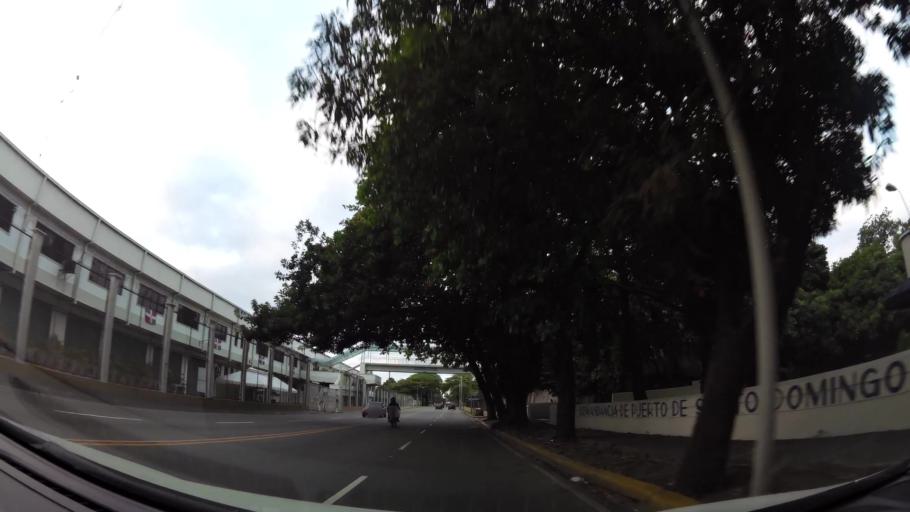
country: DO
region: Nacional
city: Ciudad Nueva
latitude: 18.4704
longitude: -69.8826
